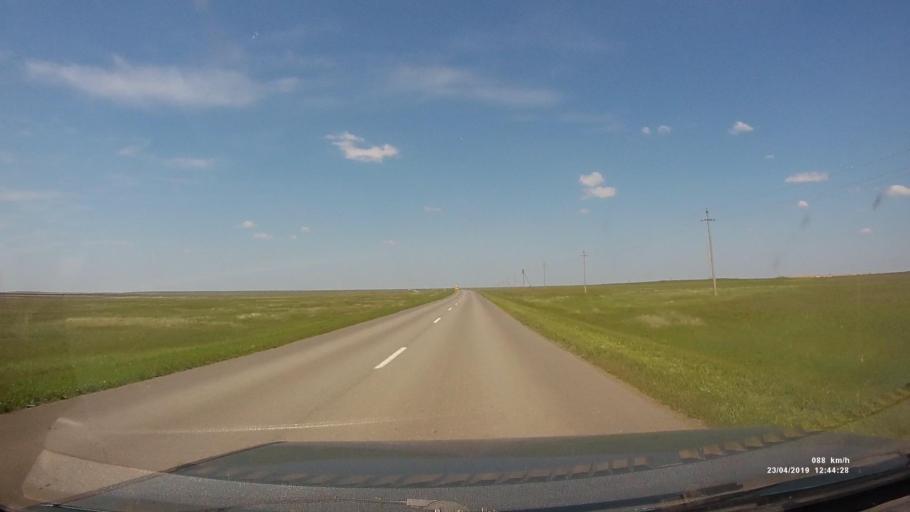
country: RU
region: Kalmykiya
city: Yashalta
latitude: 46.4773
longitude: 42.6473
